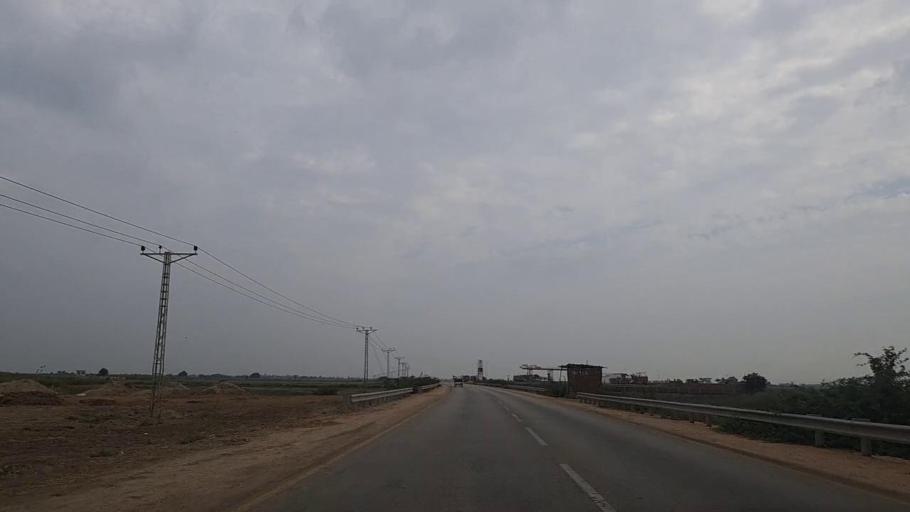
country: PK
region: Sindh
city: Thatta
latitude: 24.6154
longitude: 68.0577
